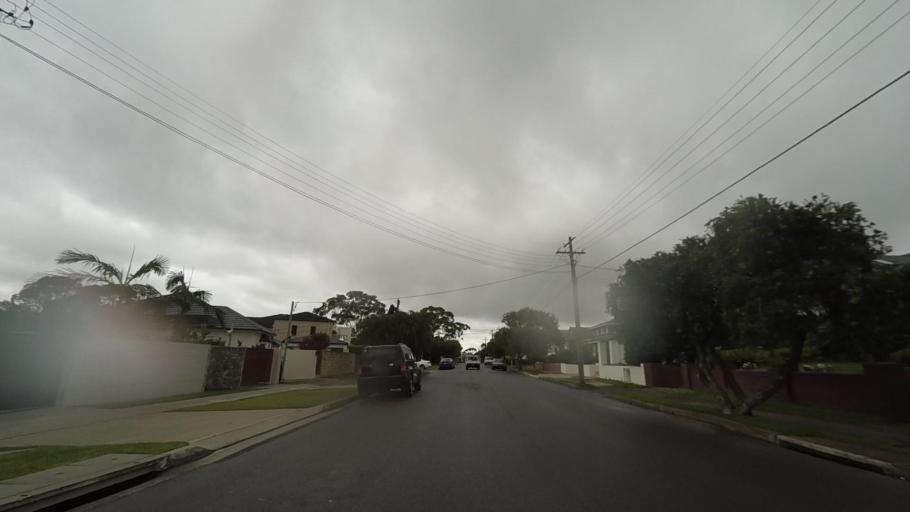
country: AU
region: New South Wales
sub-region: Kogarah
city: Kogarah
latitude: -33.9979
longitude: 151.1242
